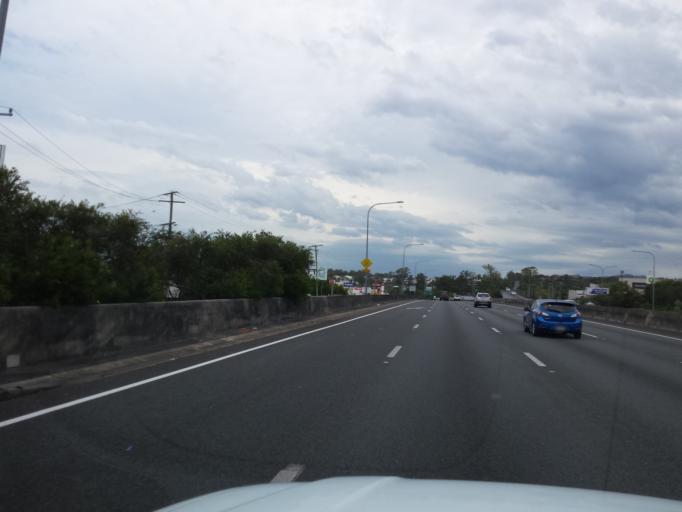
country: AU
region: Queensland
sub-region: Gold Coast
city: Nerang
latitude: -27.9978
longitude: 153.3399
